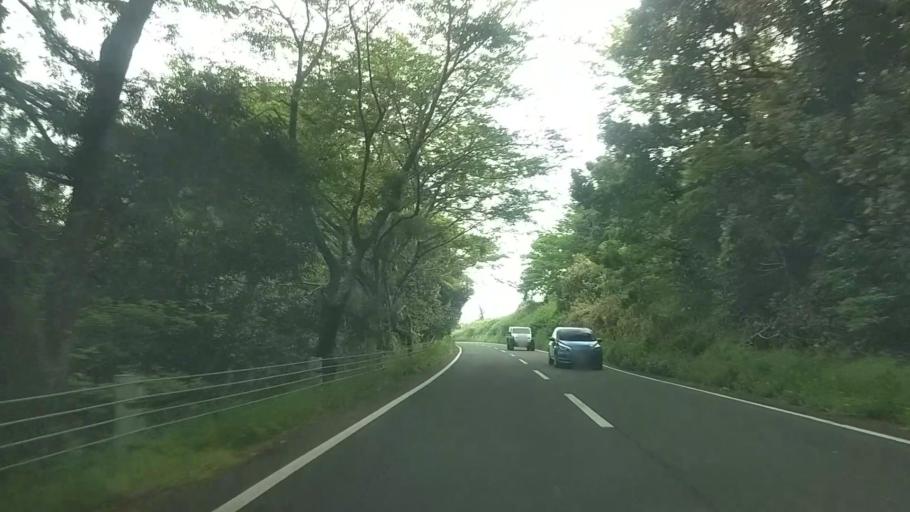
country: JP
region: Shizuoka
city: Kosai-shi
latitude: 34.7419
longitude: 137.5974
